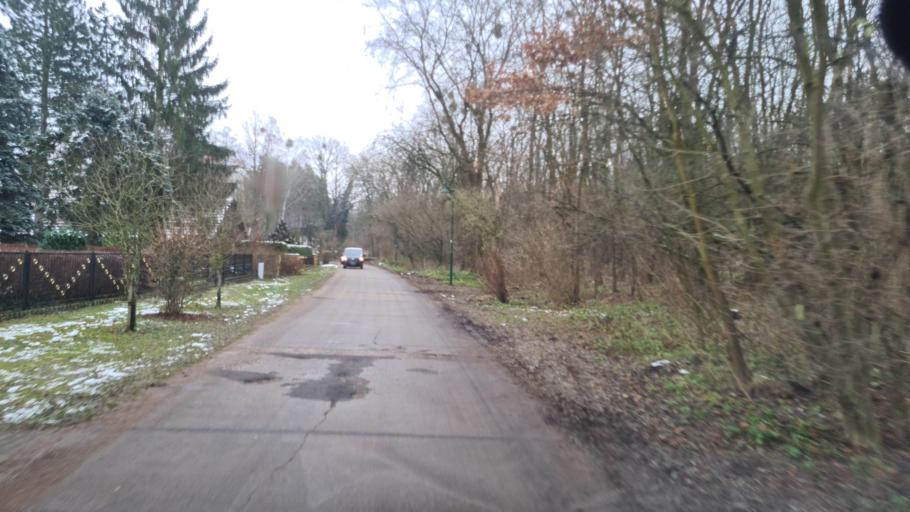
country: DE
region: Brandenburg
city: Rehfelde
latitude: 52.4555
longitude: 13.9126
